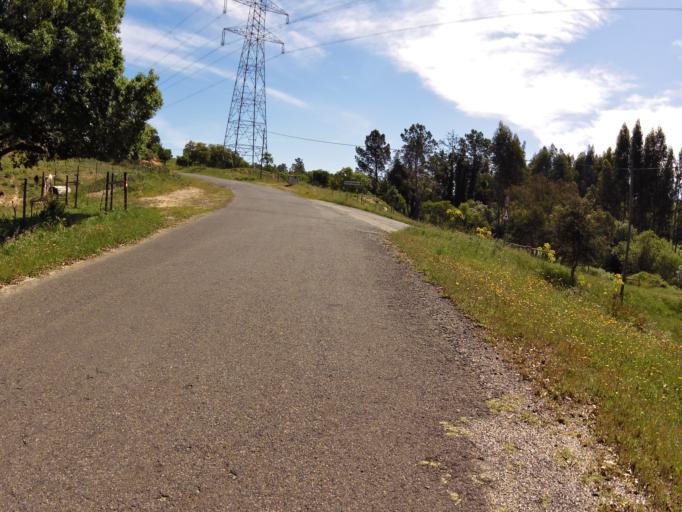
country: PT
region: Setubal
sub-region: Sines
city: Porto Covo
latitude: 37.9343
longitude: -8.7590
